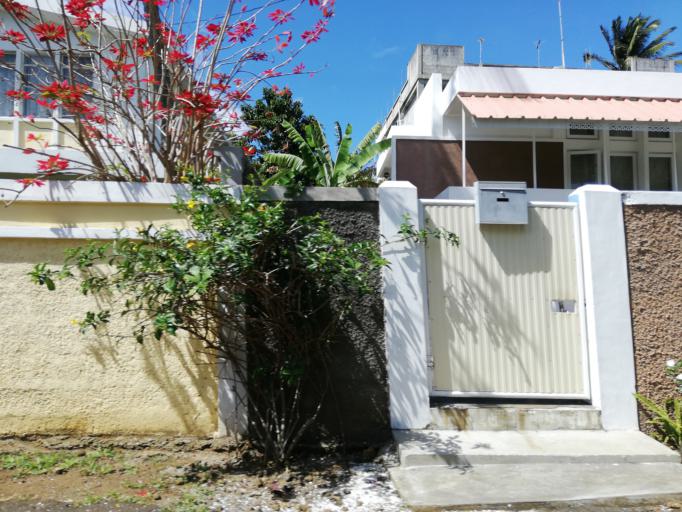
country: MU
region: Plaines Wilhems
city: Ebene
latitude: -20.2354
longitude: 57.4647
